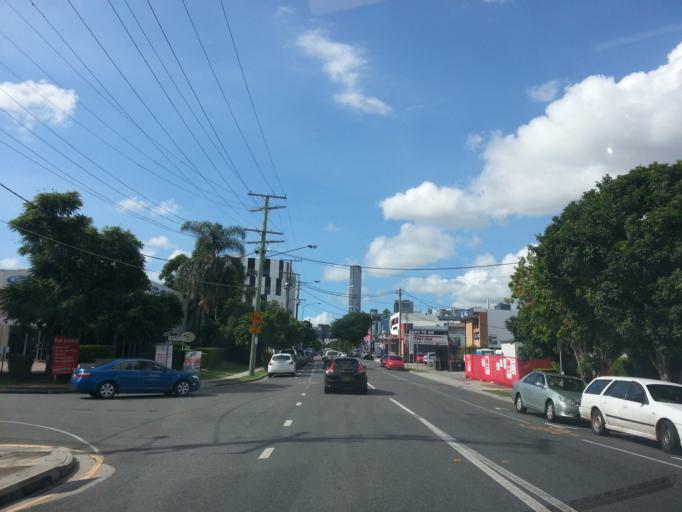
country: AU
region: Queensland
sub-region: Brisbane
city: Milton
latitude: -27.4779
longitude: 153.0070
